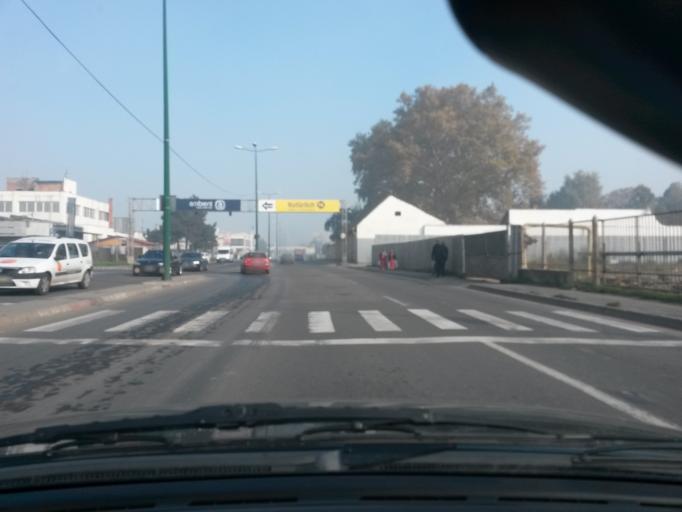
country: RO
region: Mures
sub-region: Comuna Sancraiu de Mures
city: Nazna
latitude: 46.5196
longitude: 24.5269
